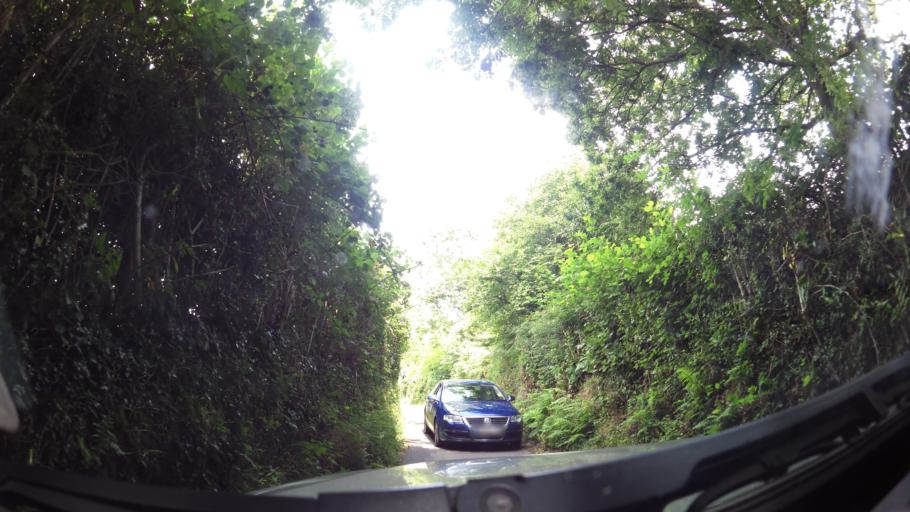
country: GB
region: Wales
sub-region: Caerphilly County Borough
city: Abertridwr
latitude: 51.5755
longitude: -3.2785
